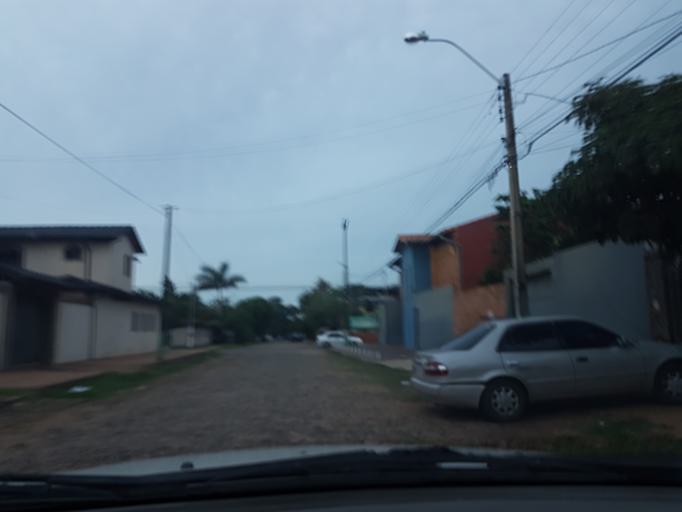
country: PY
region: Central
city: Colonia Mariano Roque Alonso
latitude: -25.2347
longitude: -57.5338
